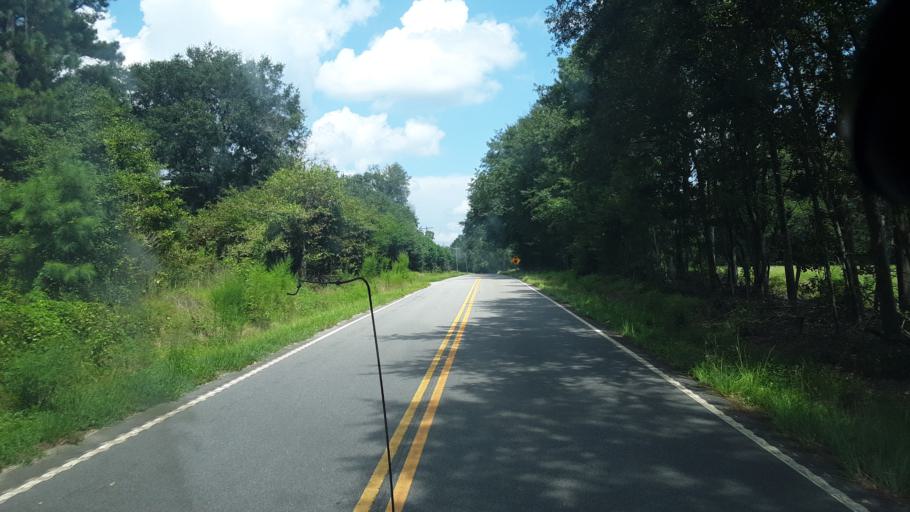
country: US
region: South Carolina
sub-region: Calhoun County
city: Oak Grove
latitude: 33.7086
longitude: -80.9544
